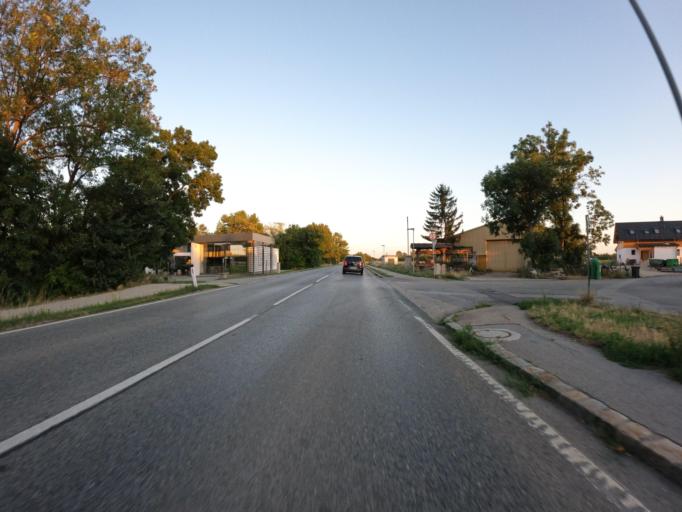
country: AT
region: Lower Austria
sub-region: Politischer Bezirk Baden
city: Pfaffstatten
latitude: 47.9994
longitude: 16.2698
